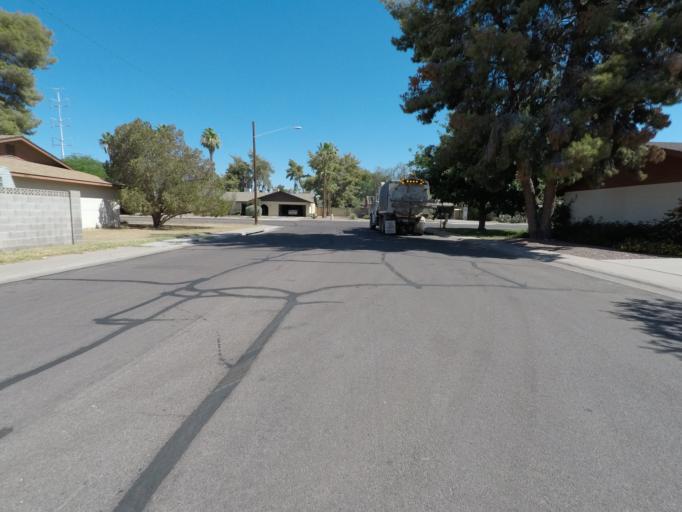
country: US
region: Arizona
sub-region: Maricopa County
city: Tempe Junction
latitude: 33.3997
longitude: -111.9426
